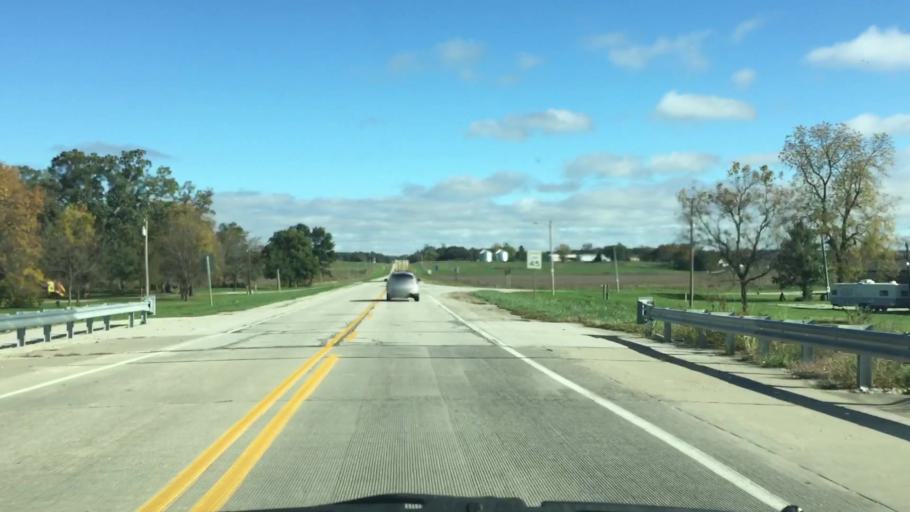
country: US
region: Iowa
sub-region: Decatur County
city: Leon
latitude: 40.6413
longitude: -93.8074
